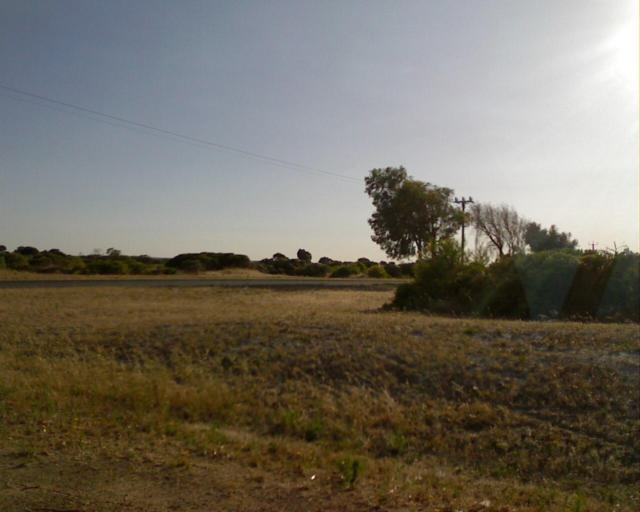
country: AU
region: Western Australia
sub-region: Dandaragan
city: Jurien Bay
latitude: -30.0524
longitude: 114.9715
